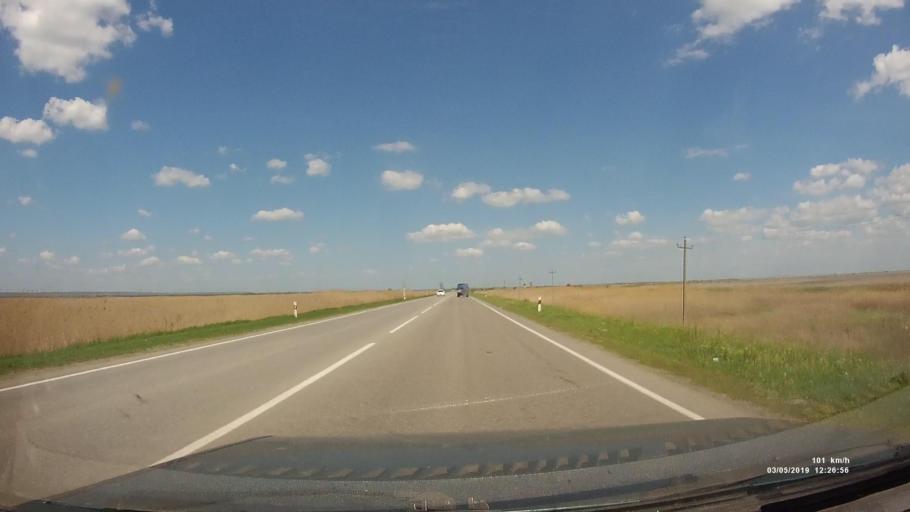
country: RU
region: Rostov
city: Semikarakorsk
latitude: 47.4533
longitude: 40.7169
